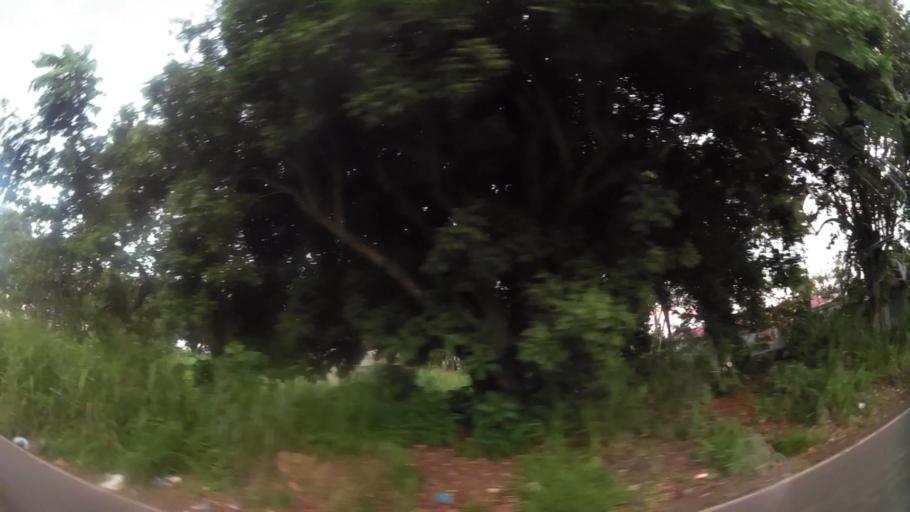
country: PA
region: Panama
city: La Chorrera
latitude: 8.8637
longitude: -79.7659
